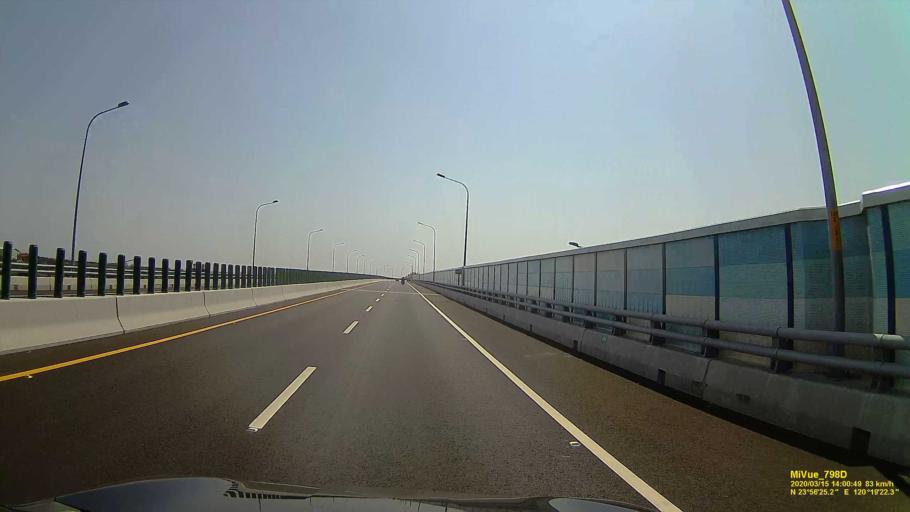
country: TW
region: Taiwan
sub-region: Changhua
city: Chang-hua
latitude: 23.9400
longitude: 120.3227
